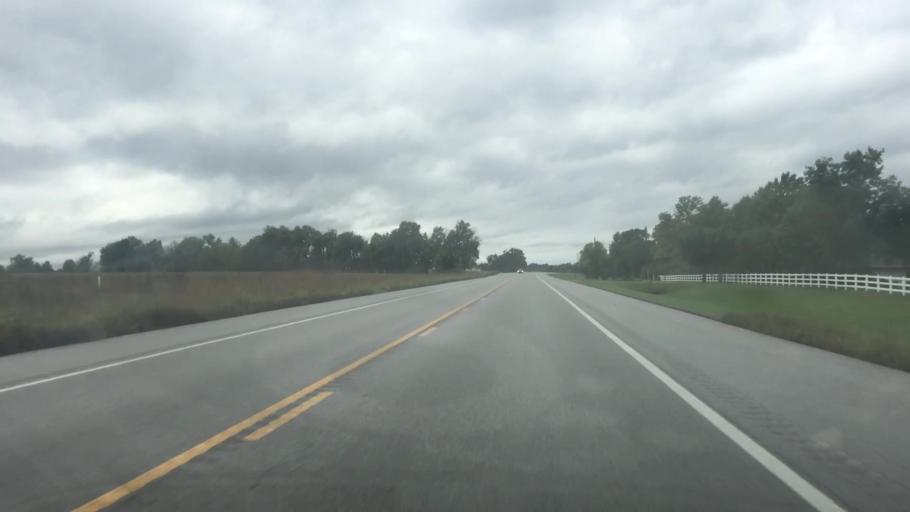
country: US
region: Kansas
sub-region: Miami County
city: Osawatomie
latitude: 38.4477
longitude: -94.9806
